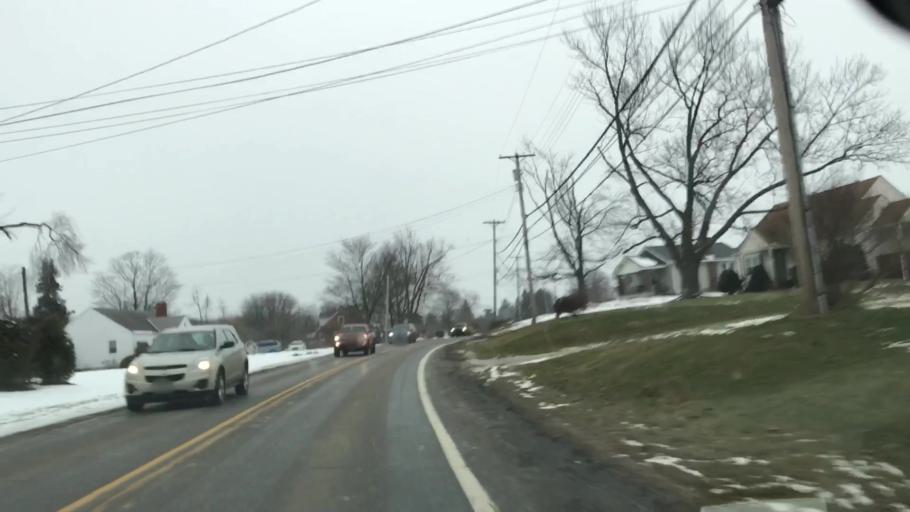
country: US
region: Pennsylvania
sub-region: Beaver County
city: Industry
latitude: 40.6993
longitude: -80.3934
